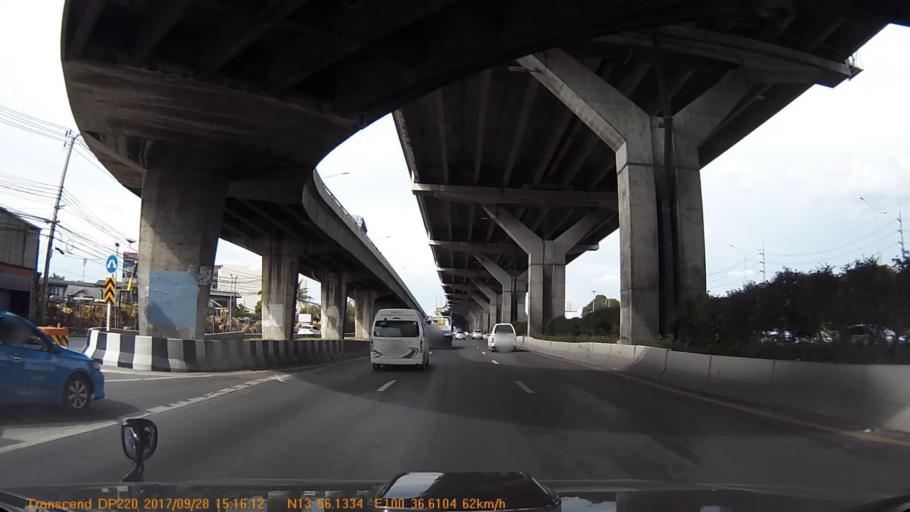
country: TH
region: Bangkok
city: Don Mueang
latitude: 13.9357
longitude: 100.6102
